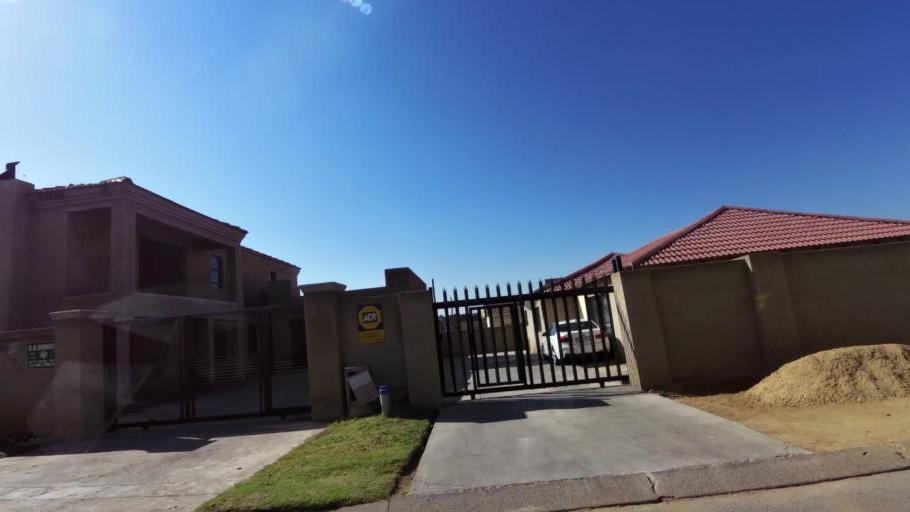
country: ZA
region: Gauteng
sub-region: City of Johannesburg Metropolitan Municipality
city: Johannesburg
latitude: -26.2512
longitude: 27.9860
